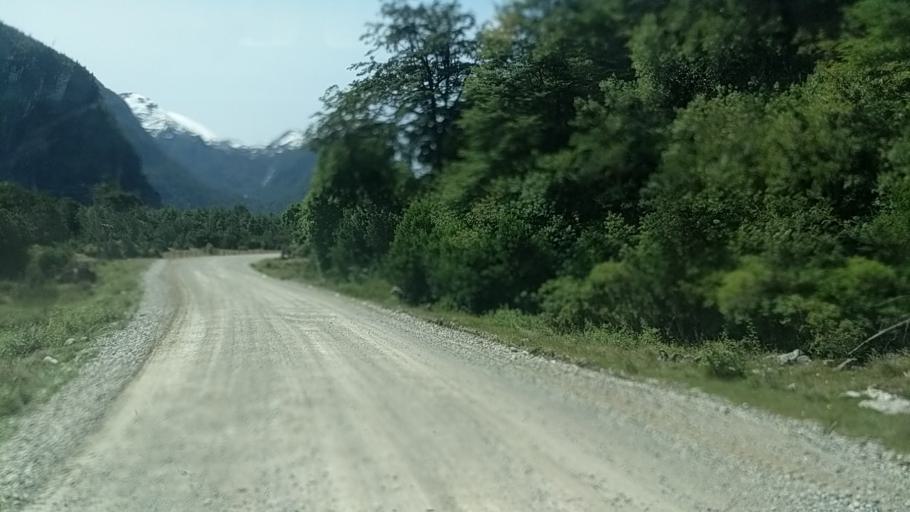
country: CL
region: Los Lagos
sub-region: Provincia de Palena
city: Palena
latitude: -43.4659
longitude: -72.1087
